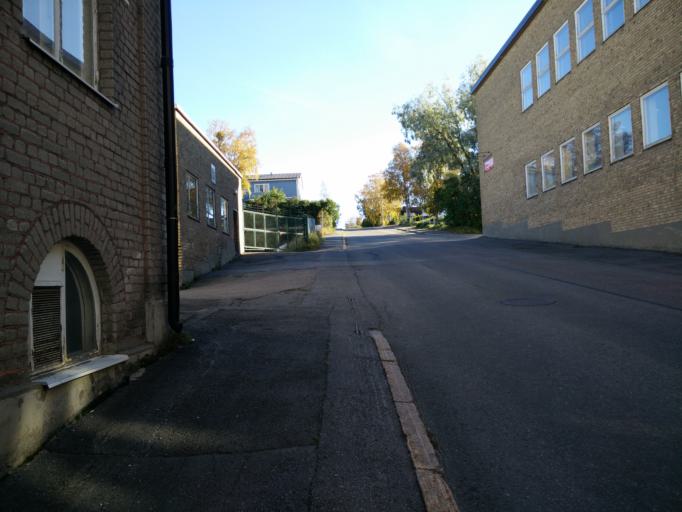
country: SE
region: Vaesternorrland
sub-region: Haernoesands Kommun
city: Haernoesand
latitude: 62.6404
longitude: 17.9528
